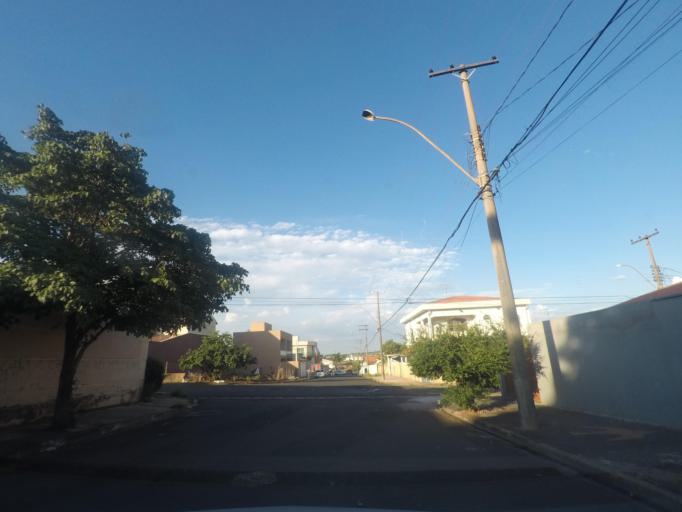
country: BR
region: Sao Paulo
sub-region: Sumare
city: Sumare
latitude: -22.8169
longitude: -47.2848
